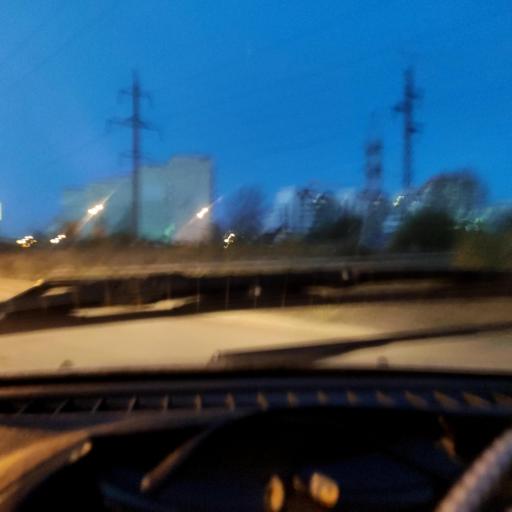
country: RU
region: Samara
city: Zhigulevsk
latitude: 53.4712
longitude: 49.5167
